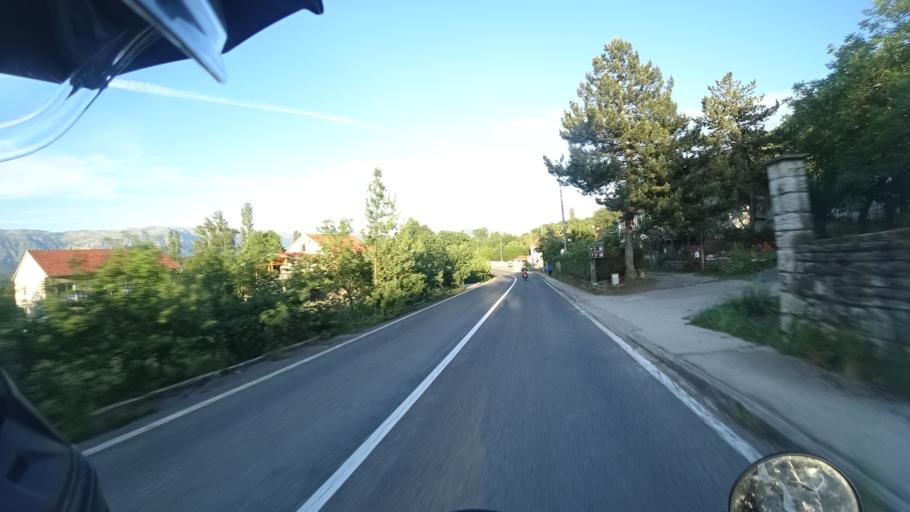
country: HR
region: Splitsko-Dalmatinska
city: Hrvace
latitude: 43.9039
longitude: 16.4082
